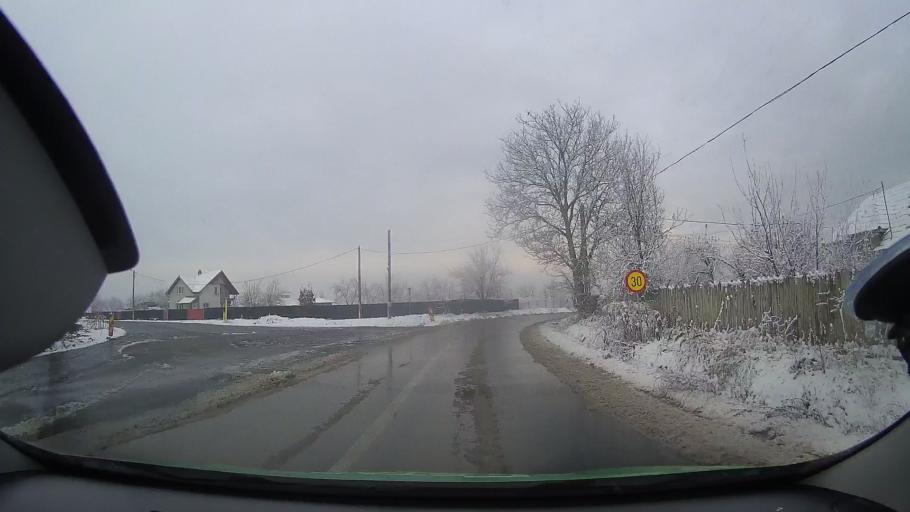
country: RO
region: Mures
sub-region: Comuna Bogata
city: Bogata
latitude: 46.4537
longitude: 24.0820
